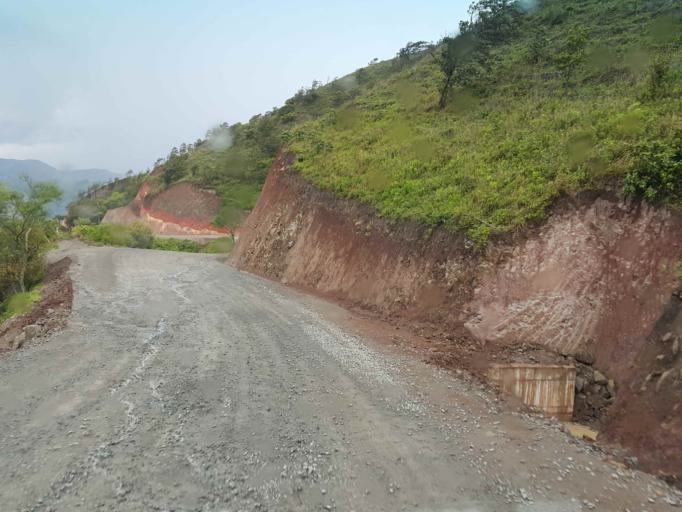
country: CR
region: Guanacaste
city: Juntas
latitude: 10.2709
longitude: -84.8372
